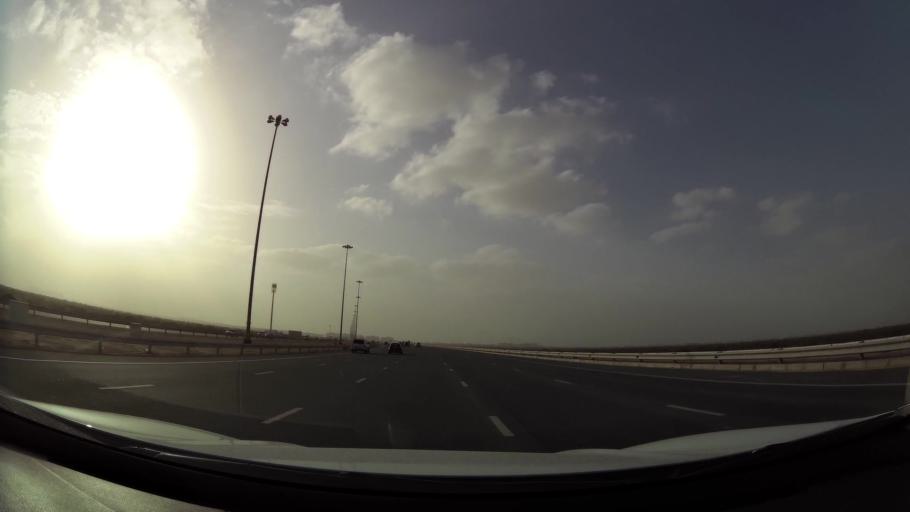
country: AE
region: Abu Dhabi
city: Abu Dhabi
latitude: 24.5458
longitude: 54.4767
